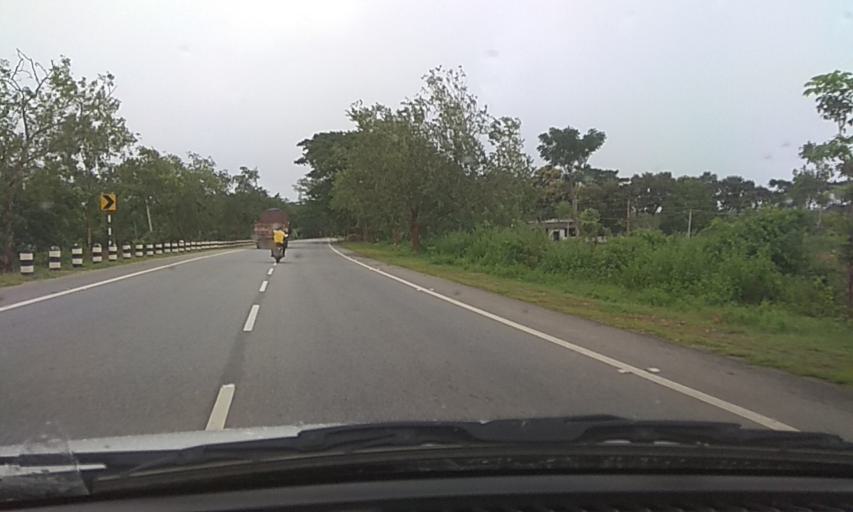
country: IN
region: Karnataka
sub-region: Mandya
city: Maddur
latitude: 12.7952
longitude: 77.0434
